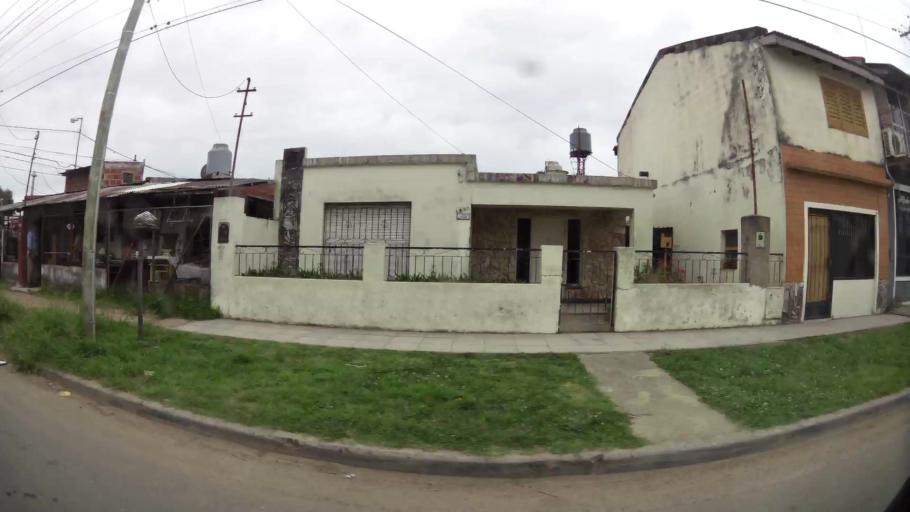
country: AR
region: Buenos Aires
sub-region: Partido de Zarate
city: Zarate
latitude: -34.1108
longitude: -59.0272
